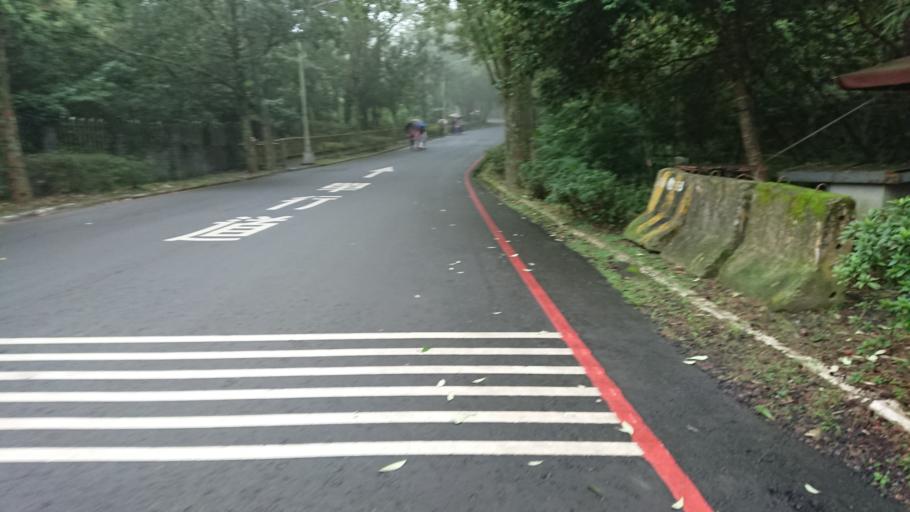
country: TW
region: Taiwan
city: Daxi
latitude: 24.8172
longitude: 121.2405
